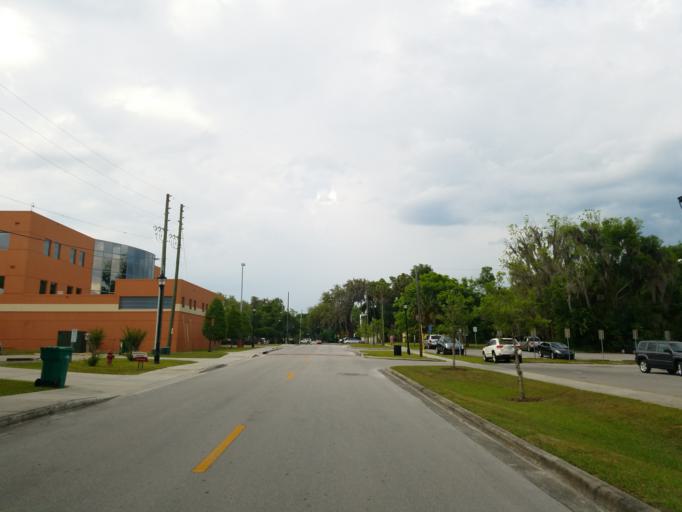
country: US
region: Florida
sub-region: Citrus County
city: Inverness
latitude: 28.8362
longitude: -82.3289
